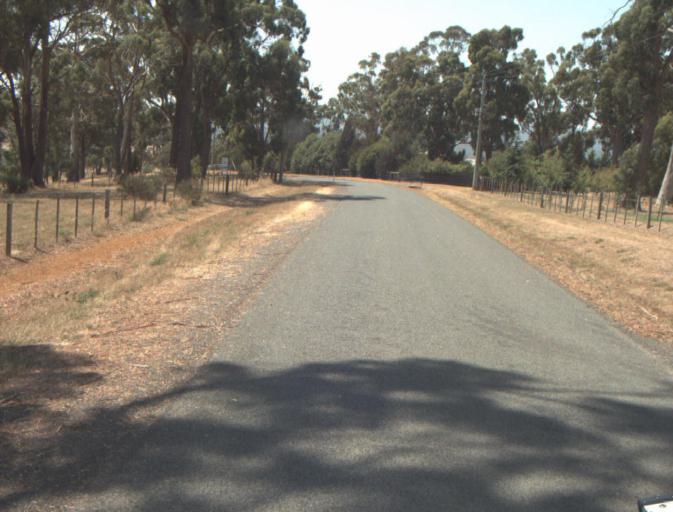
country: AU
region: Tasmania
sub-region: Launceston
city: Newstead
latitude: -41.4995
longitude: 147.2114
